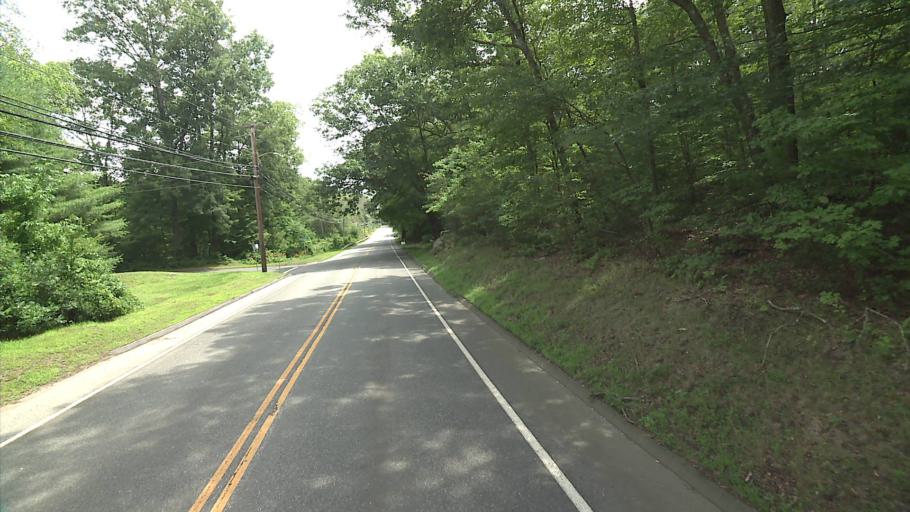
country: US
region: Connecticut
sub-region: New Haven County
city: Guilford
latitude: 41.3533
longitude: -72.6738
